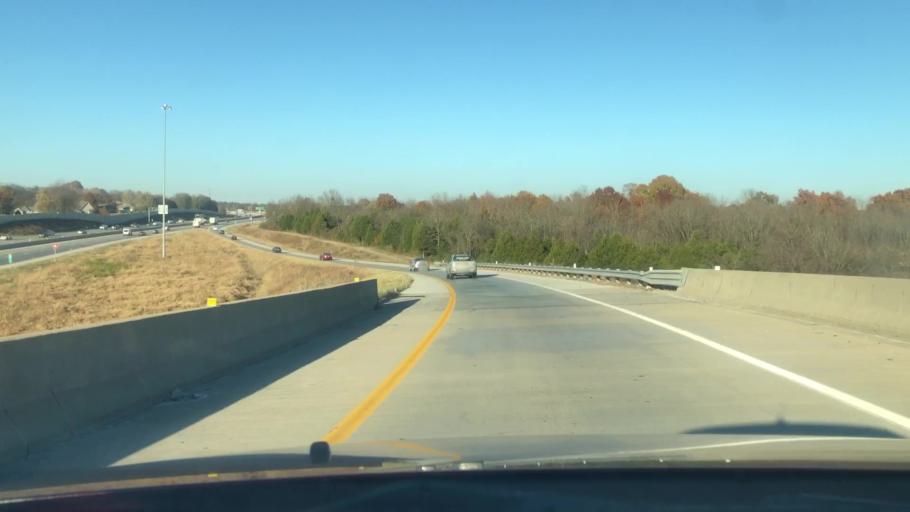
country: US
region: Missouri
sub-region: Christian County
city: Nixa
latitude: 37.1293
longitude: -93.2286
